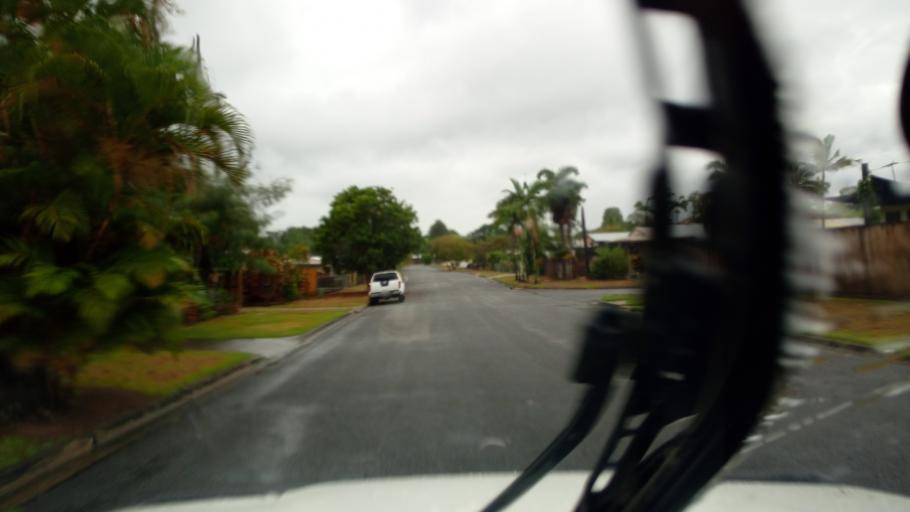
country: AU
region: Queensland
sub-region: Cairns
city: Woree
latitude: -16.9386
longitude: 145.7320
